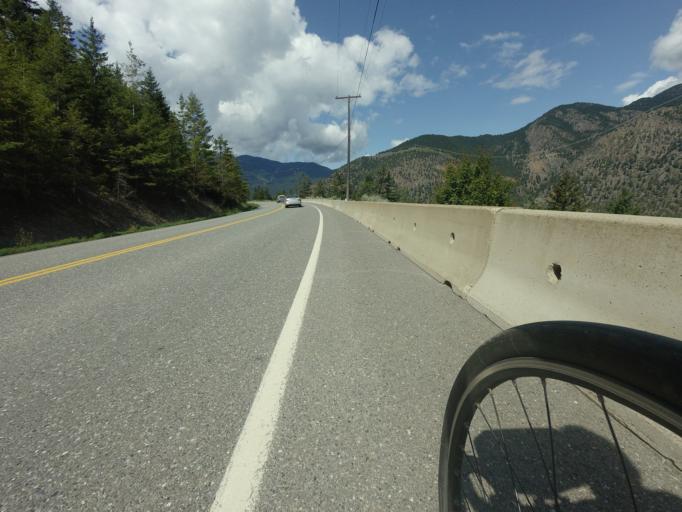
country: CA
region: British Columbia
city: Lillooet
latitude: 50.7597
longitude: -121.9094
